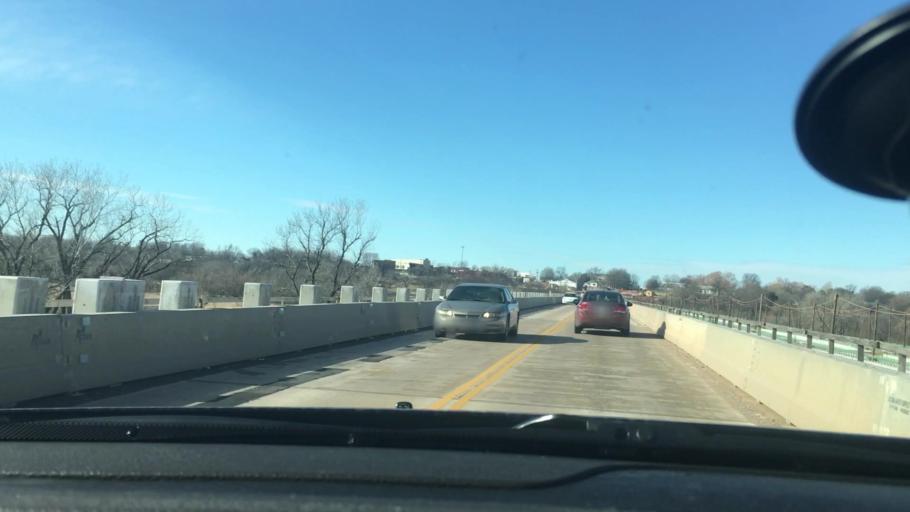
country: US
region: Oklahoma
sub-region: McClain County
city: Purcell
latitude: 35.0142
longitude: -97.3518
